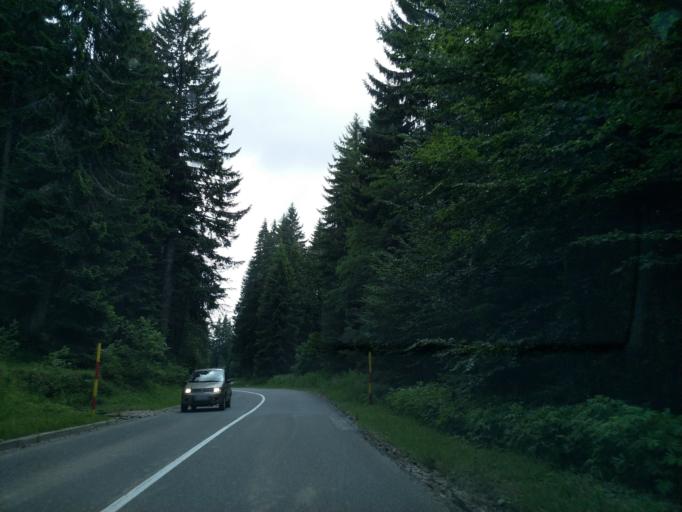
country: XK
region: Mitrovica
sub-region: Komuna e Leposaviqit
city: Leposaviq
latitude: 43.2767
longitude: 20.7934
